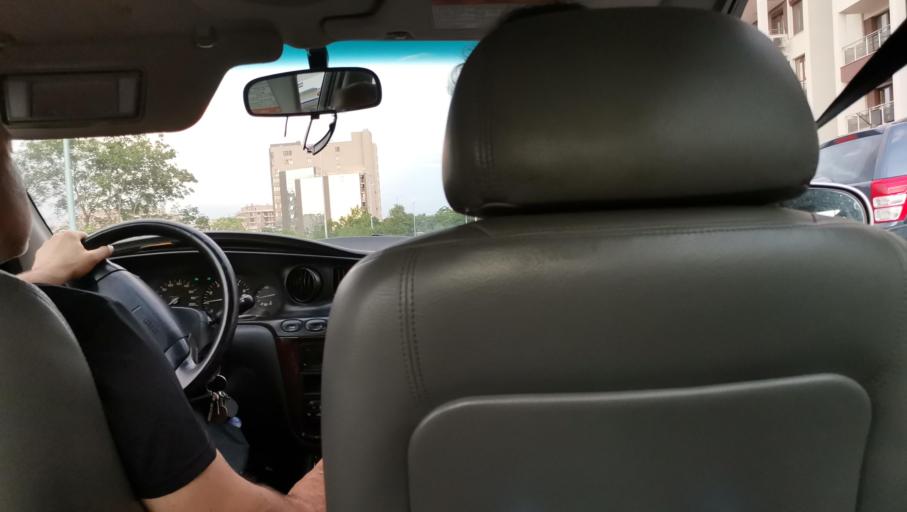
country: BG
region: Plovdiv
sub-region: Obshtina Plovdiv
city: Plovdiv
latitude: 42.1391
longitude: 24.7874
